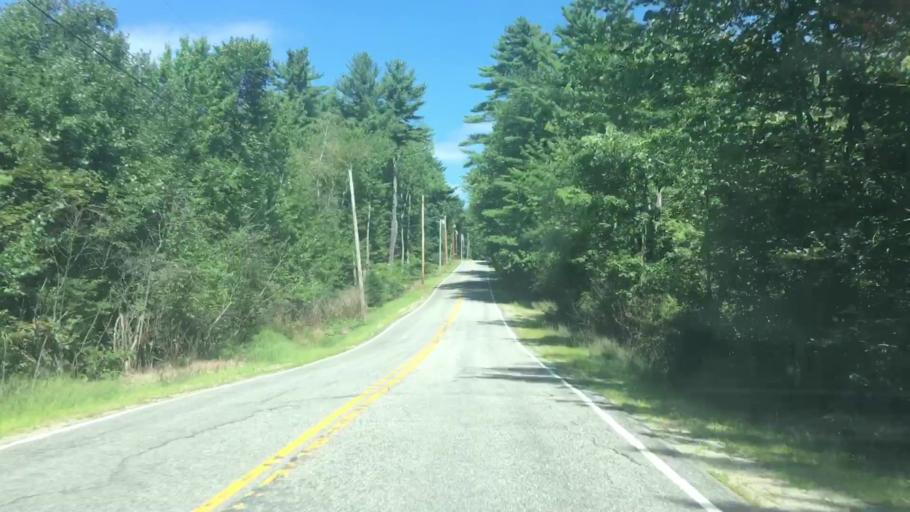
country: US
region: Maine
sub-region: Kennebec County
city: Monmouth
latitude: 44.1449
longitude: -69.9571
